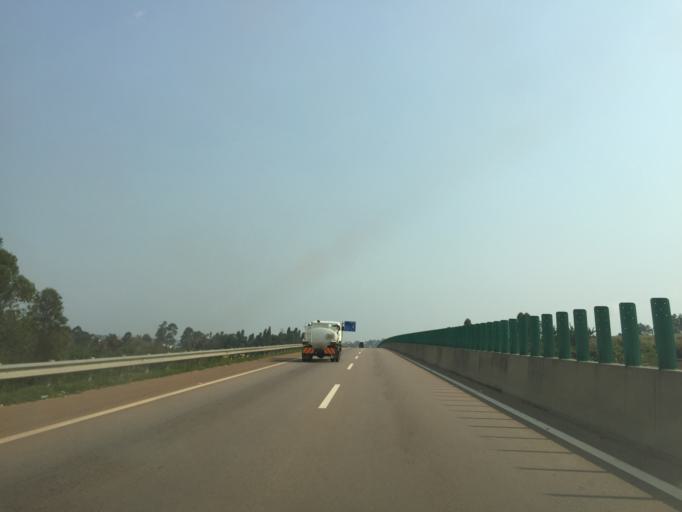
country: UG
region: Central Region
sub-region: Wakiso District
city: Kajansi
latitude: 0.2268
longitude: 32.5262
